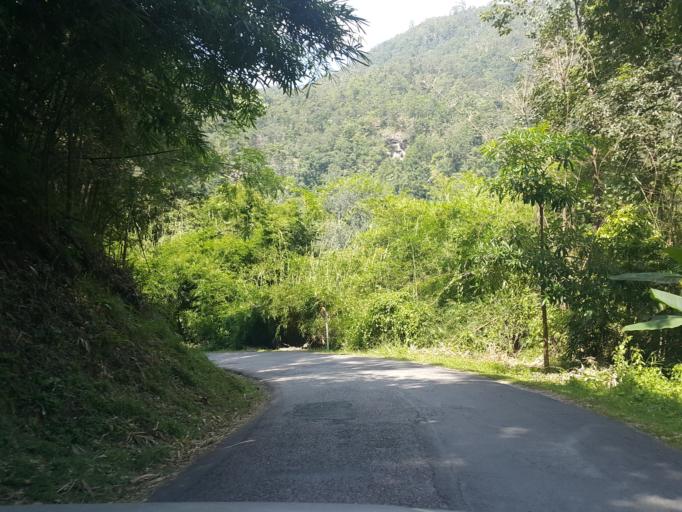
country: TH
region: Chiang Mai
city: Chom Thong
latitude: 18.5392
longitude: 98.6005
